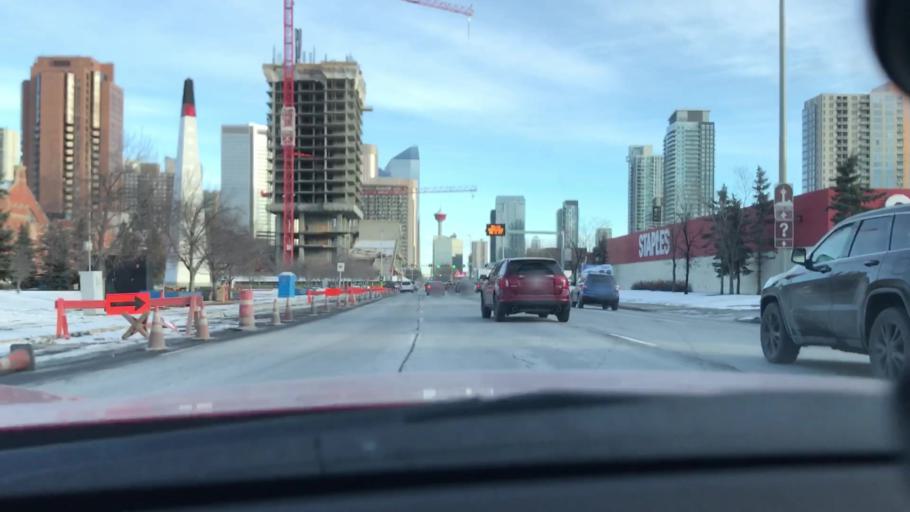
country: CA
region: Alberta
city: Calgary
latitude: 51.0455
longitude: -114.0917
